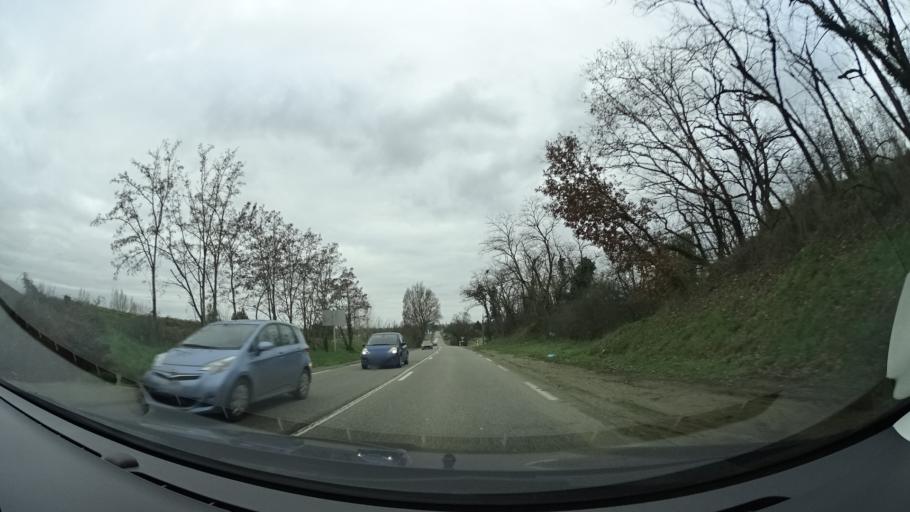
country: FR
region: Aquitaine
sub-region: Departement du Lot-et-Garonne
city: Castelmoron-sur-Lot
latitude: 44.3845
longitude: 0.5427
